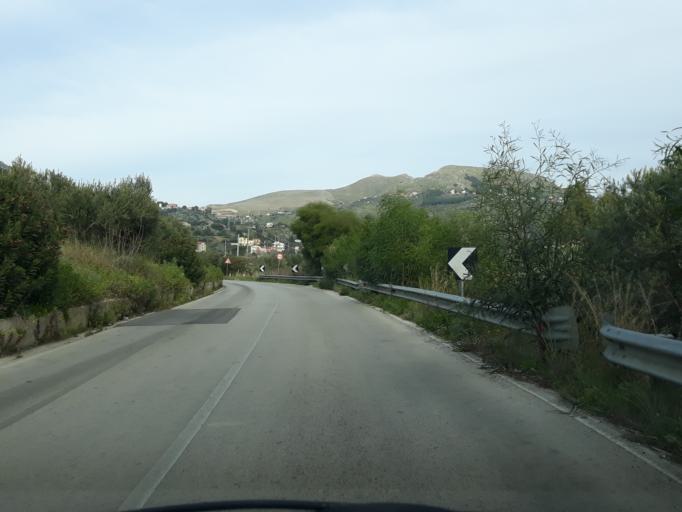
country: IT
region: Sicily
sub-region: Palermo
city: Giardinello
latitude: 38.0774
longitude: 13.1591
